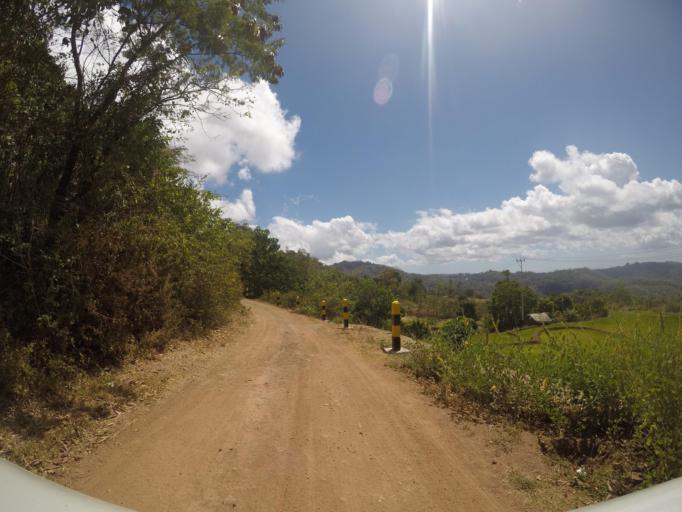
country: TL
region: Lautem
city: Lospalos
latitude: -8.5392
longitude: 126.8038
